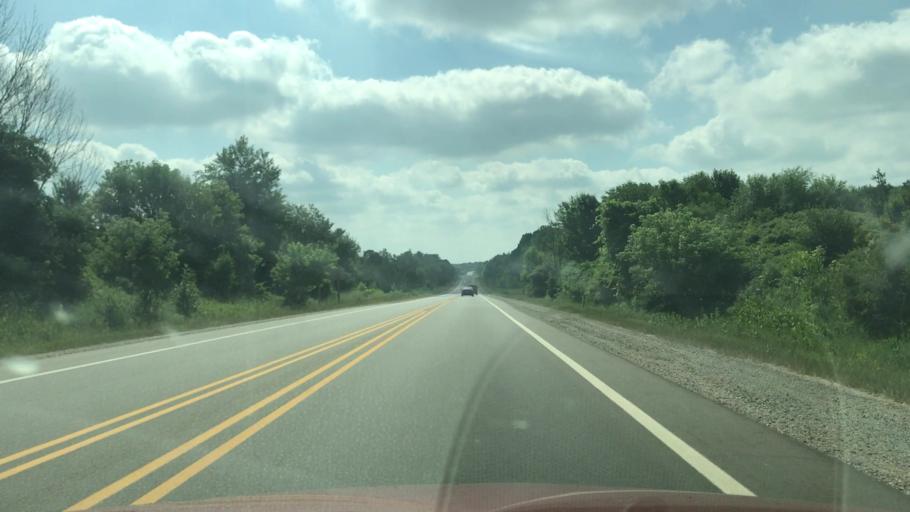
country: US
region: Michigan
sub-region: Kent County
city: Kent City
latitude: 43.2108
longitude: -85.7488
